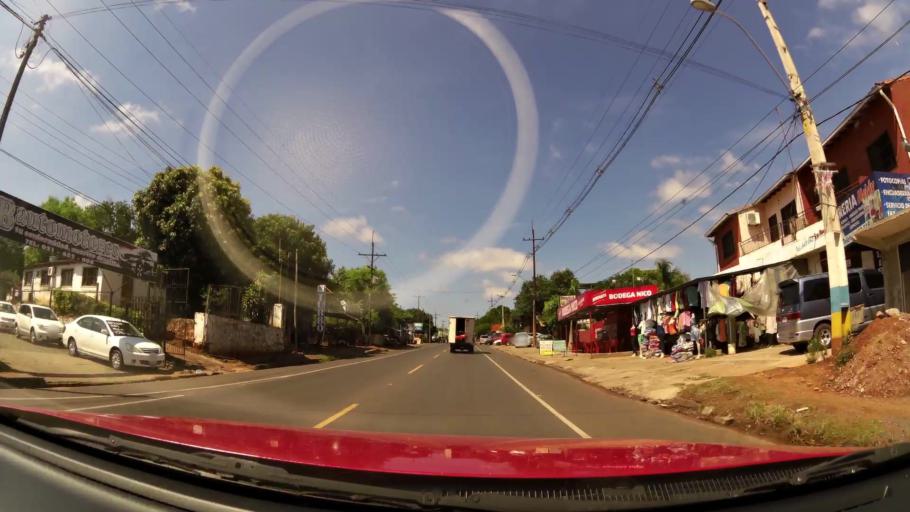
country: PY
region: Central
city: San Lorenzo
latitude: -25.3090
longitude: -57.5057
